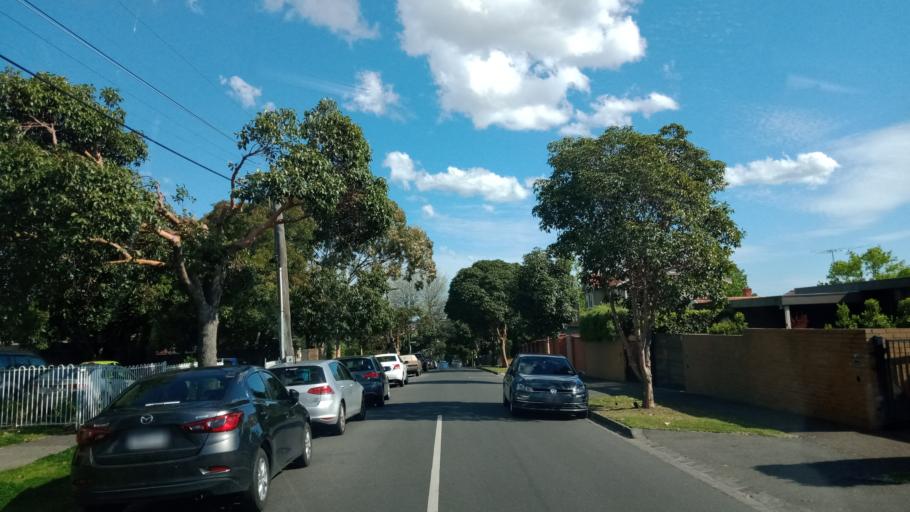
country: AU
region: Victoria
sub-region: Boroondara
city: Camberwell
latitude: -37.8462
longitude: 145.0568
